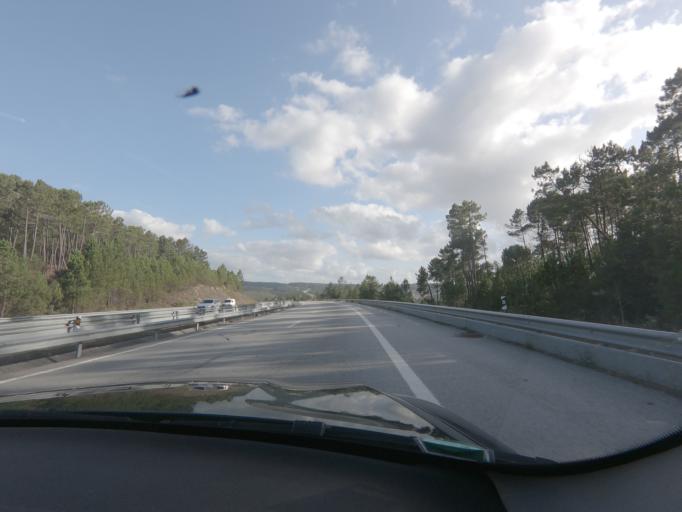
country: PT
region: Viseu
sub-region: Viseu
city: Campo
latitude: 40.7658
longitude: -7.9235
